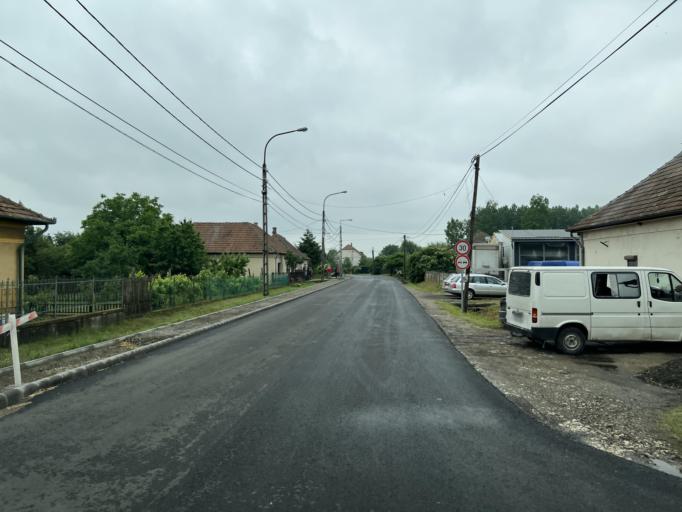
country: HU
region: Pest
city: Tura
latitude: 47.6253
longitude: 19.5968
